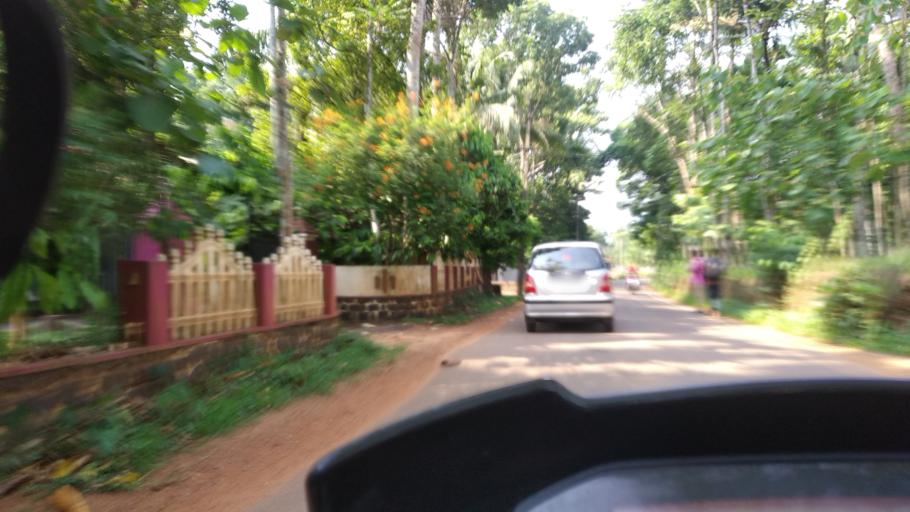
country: IN
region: Kerala
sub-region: Ernakulam
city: Piravam
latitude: 9.8432
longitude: 76.5355
